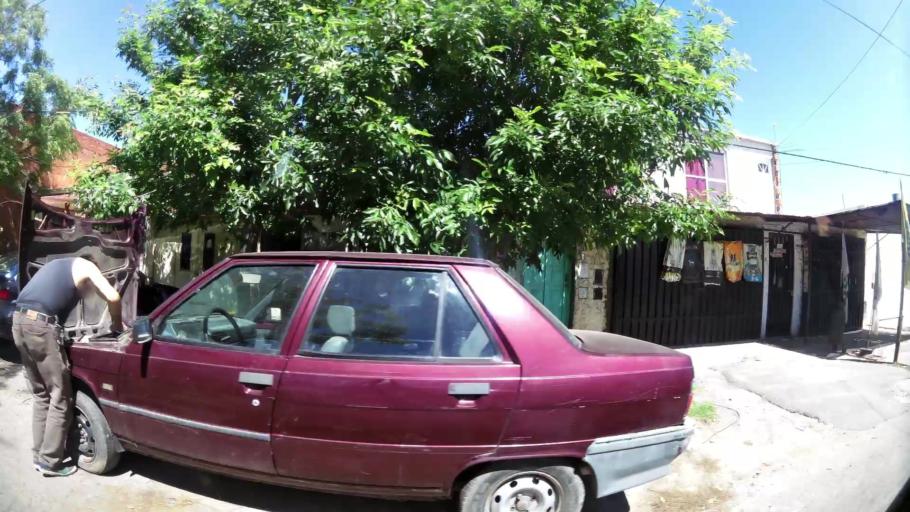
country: AR
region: Santa Fe
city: Perez
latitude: -32.9664
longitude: -60.7153
